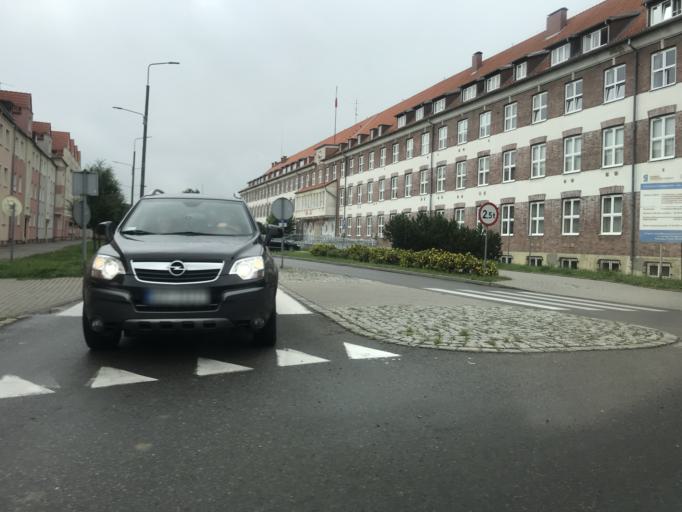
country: PL
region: Warmian-Masurian Voivodeship
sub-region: Powiat elblaski
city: Elblag
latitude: 54.1555
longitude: 19.4199
